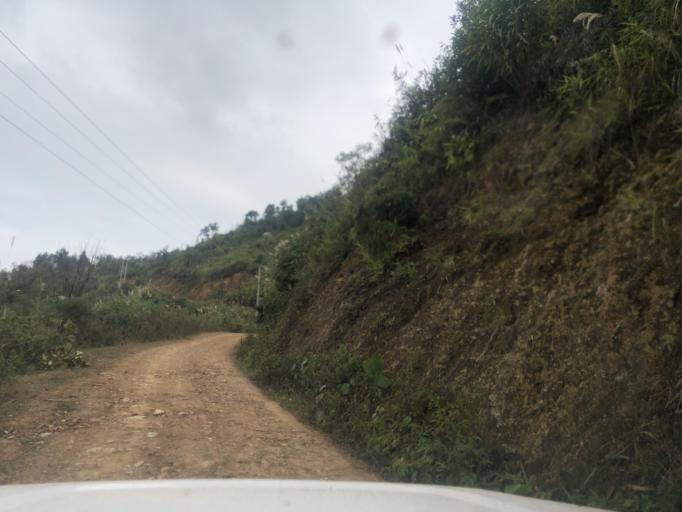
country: LA
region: Phongsali
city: Khoa
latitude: 21.2540
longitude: 102.5889
